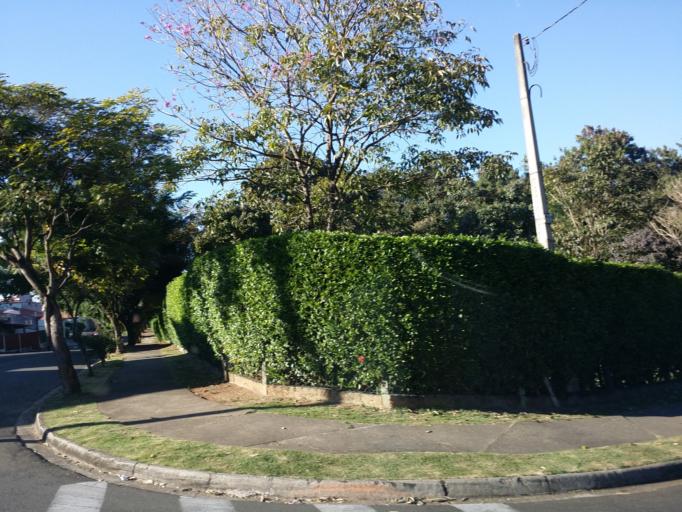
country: BR
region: Sao Paulo
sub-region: Indaiatuba
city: Indaiatuba
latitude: -23.0966
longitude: -47.2033
